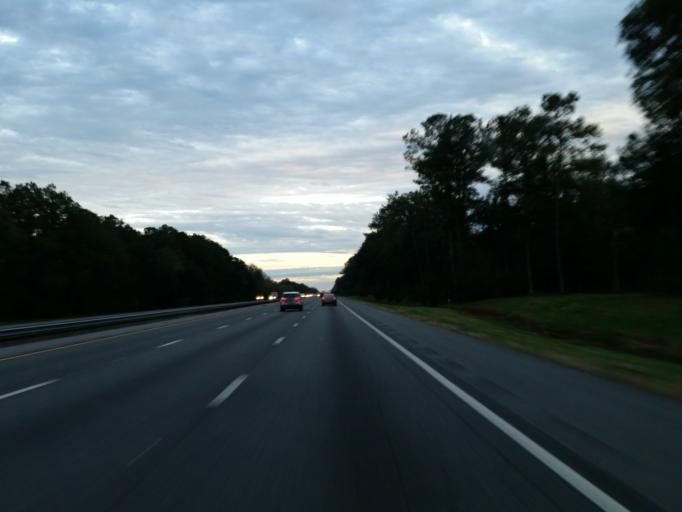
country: US
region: Florida
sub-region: Hamilton County
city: Jasper
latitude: 30.4695
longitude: -82.9674
